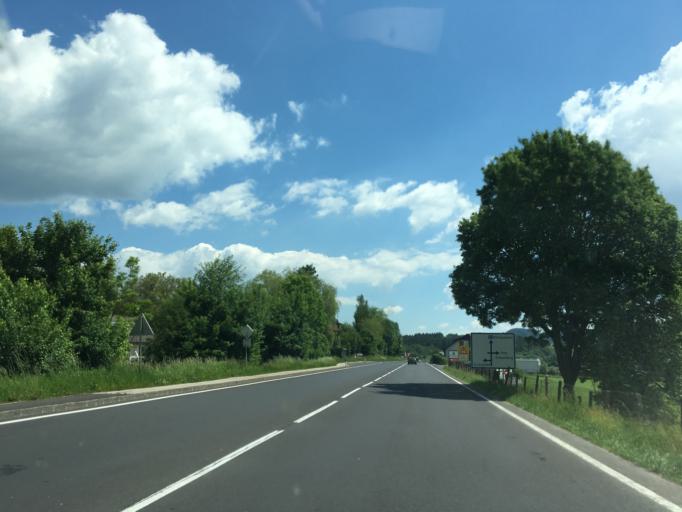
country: AT
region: Upper Austria
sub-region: Politischer Bezirk Perg
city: Perg
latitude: 48.3370
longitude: 14.5684
